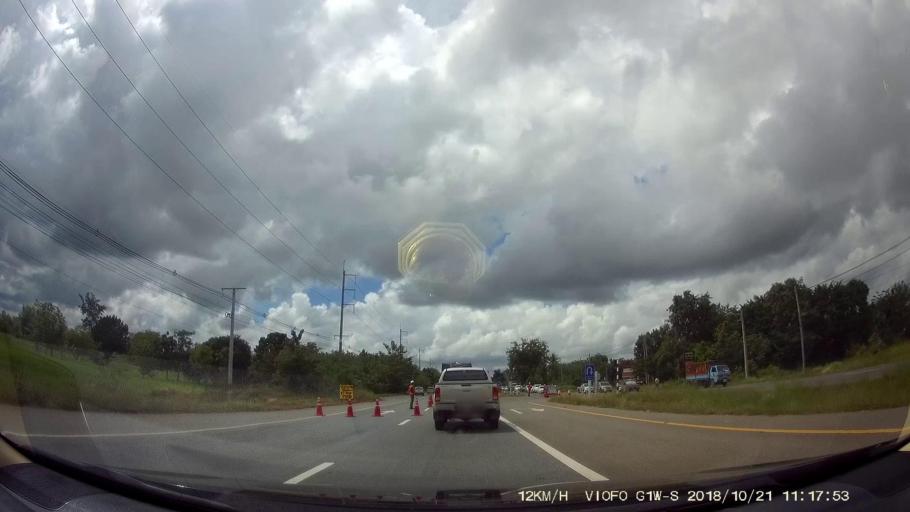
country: TH
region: Chaiyaphum
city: Chaiyaphum
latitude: 15.8794
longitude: 102.0974
